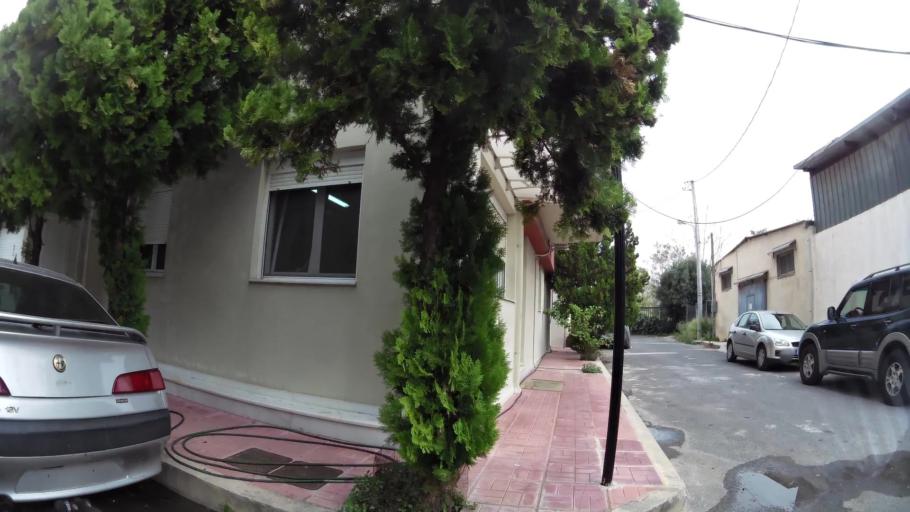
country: GR
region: Attica
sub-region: Nomarchia Athinas
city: Tavros
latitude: 37.9706
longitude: 23.6895
